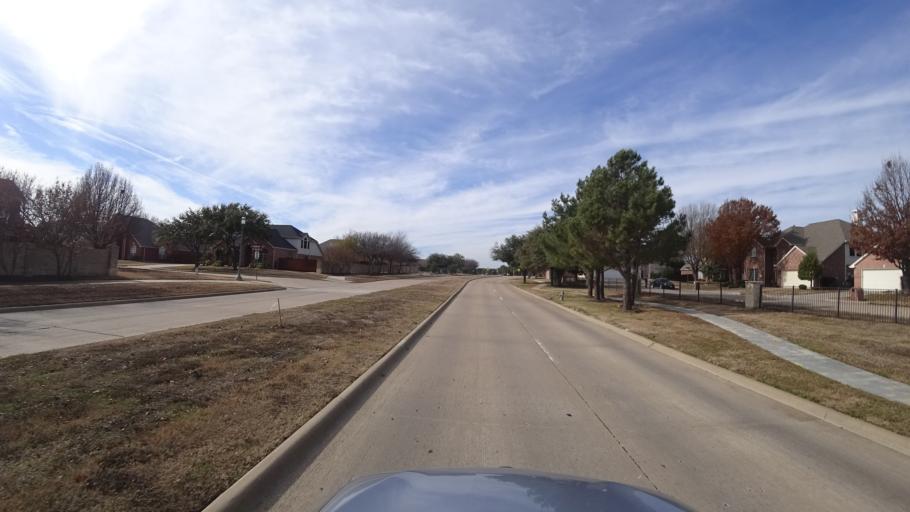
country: US
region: Texas
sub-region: Denton County
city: Highland Village
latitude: 33.0653
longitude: -97.0460
